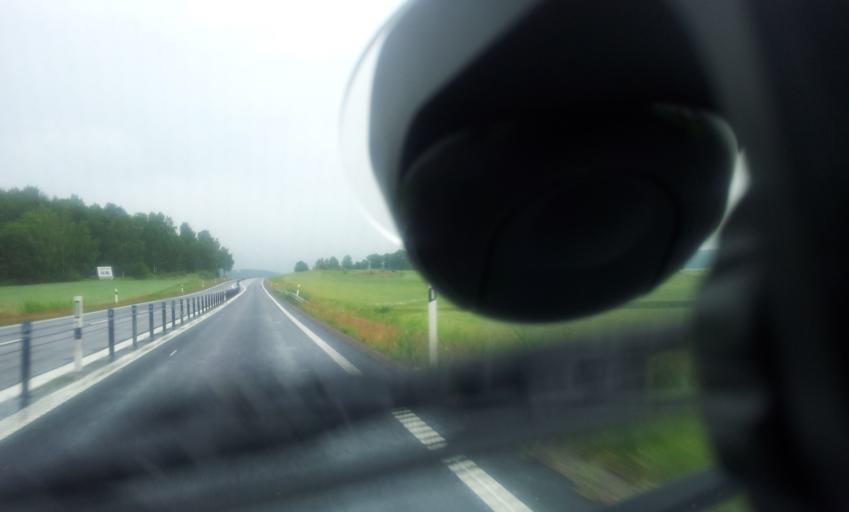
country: SE
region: OEstergoetland
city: Lindo
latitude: 58.5481
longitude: 16.2580
